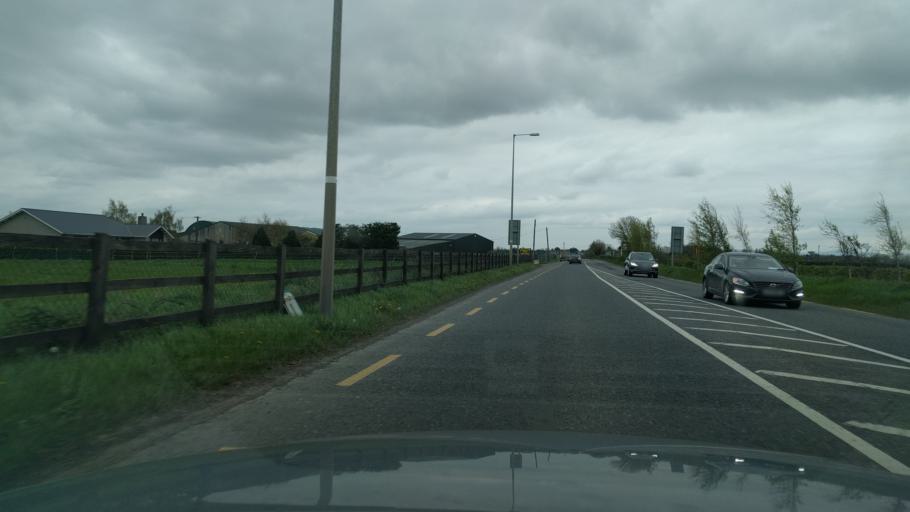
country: IE
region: Leinster
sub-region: An Mhi
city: Ashbourne
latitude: 53.4574
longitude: -6.3494
